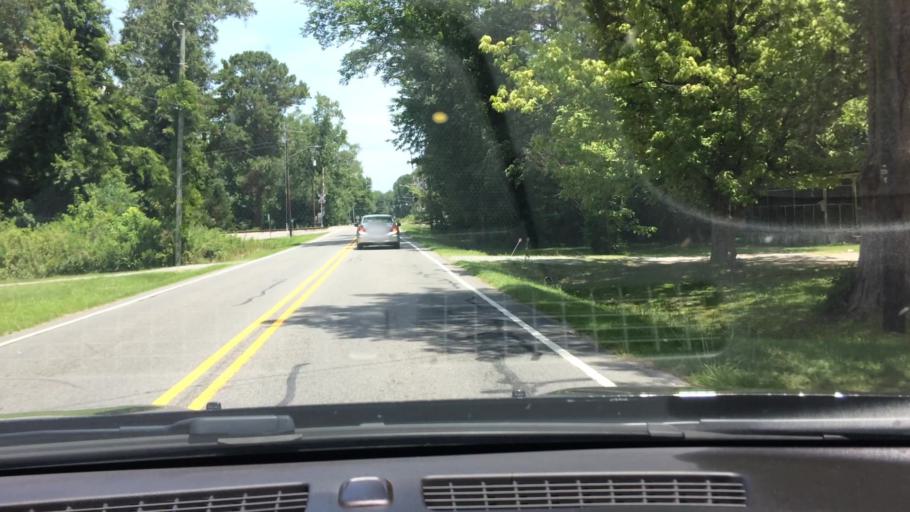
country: US
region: North Carolina
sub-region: Beaufort County
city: Washington
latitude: 35.5641
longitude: -77.1889
